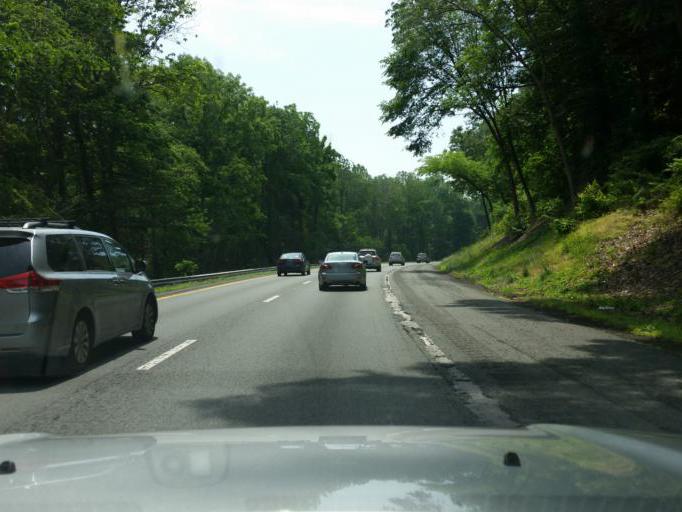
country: US
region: Maryland
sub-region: Frederick County
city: Green Valley
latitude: 39.2712
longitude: -77.3152
